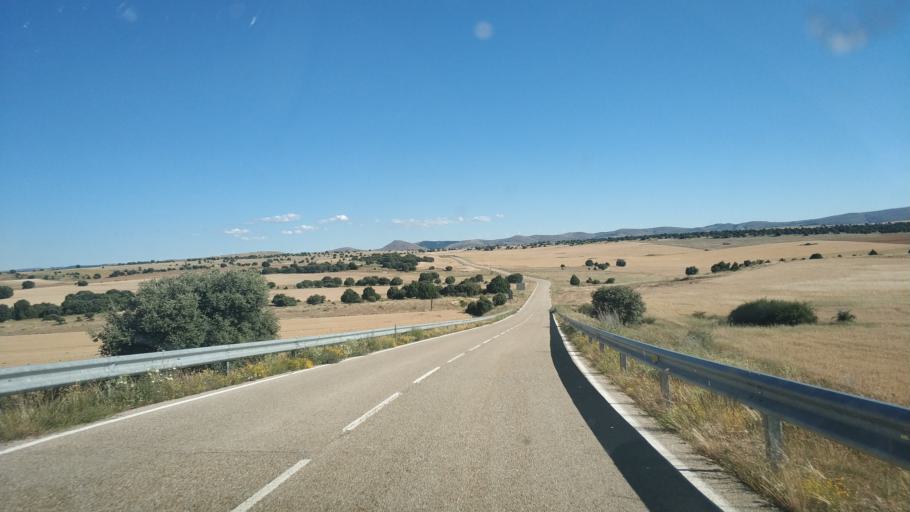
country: ES
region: Castille and Leon
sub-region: Provincia de Soria
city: Montejo de Tiermes
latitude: 41.4006
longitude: -3.1994
